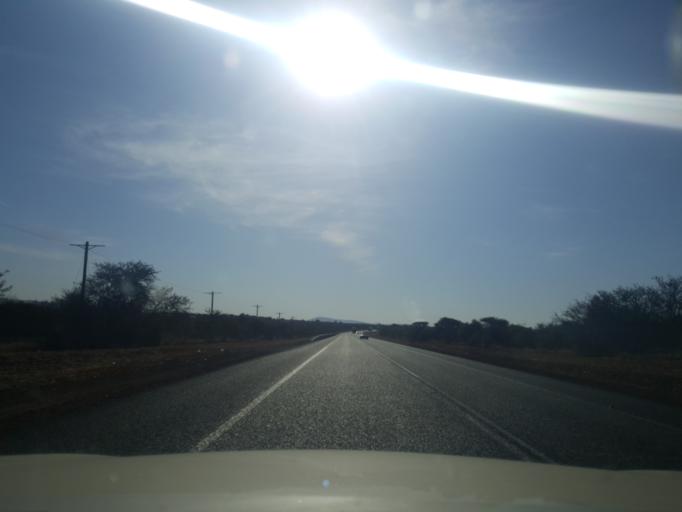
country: ZA
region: North-West
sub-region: Ngaka Modiri Molema District Municipality
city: Zeerust
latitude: -25.5198
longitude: 26.0047
